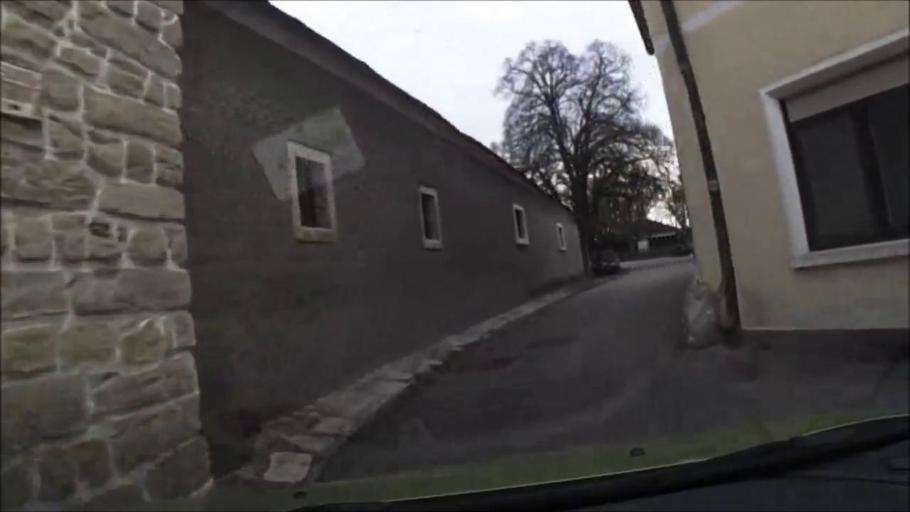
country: AT
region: Burgenland
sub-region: Eisenstadt-Umgebung
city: Loretto
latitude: 47.9146
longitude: 16.5141
